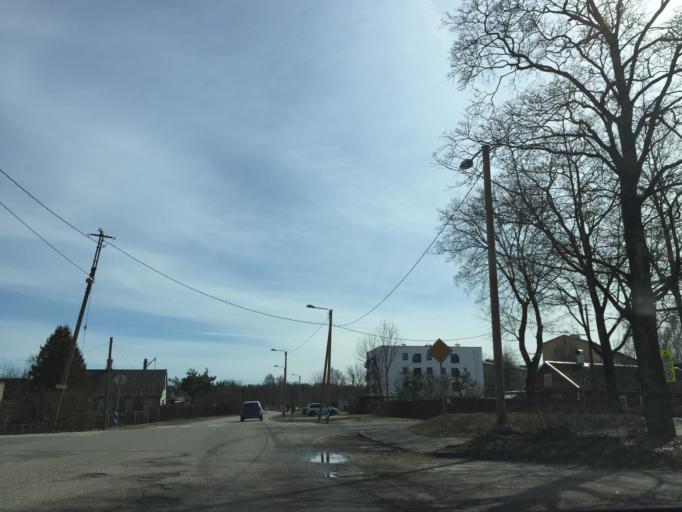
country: EE
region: Paernumaa
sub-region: Paernu linn
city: Parnu
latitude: 58.3823
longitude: 24.5289
